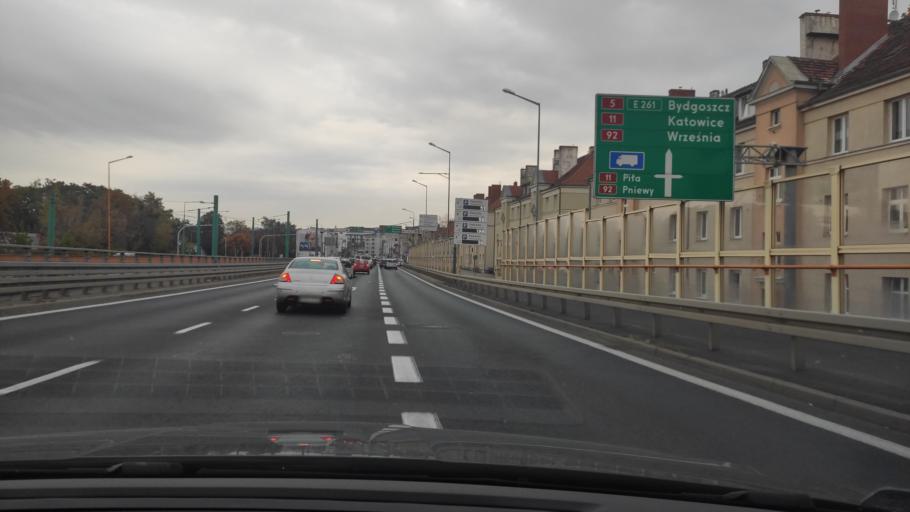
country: PL
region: Greater Poland Voivodeship
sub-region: Powiat poznanski
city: Lubon
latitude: 52.3813
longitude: 16.8827
